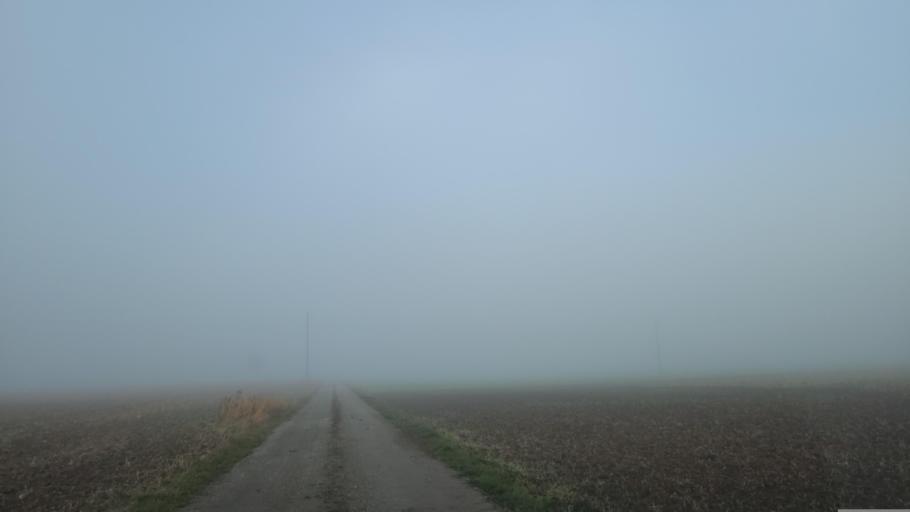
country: SE
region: Uppsala
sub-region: Enkopings Kommun
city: Grillby
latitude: 59.5987
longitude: 17.1751
